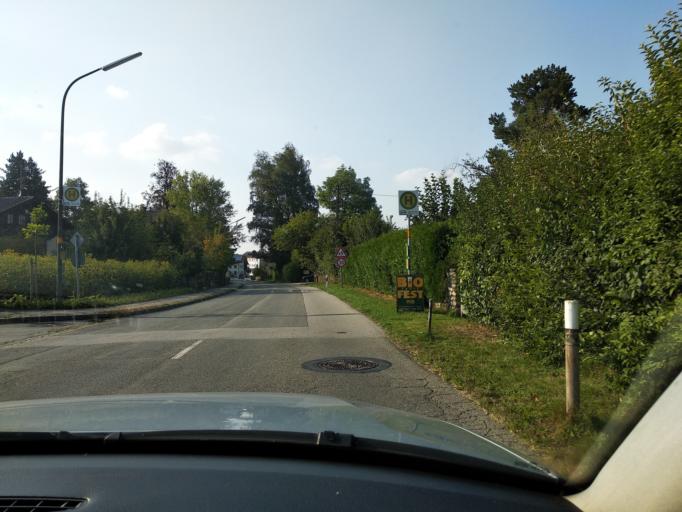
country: DE
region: Bavaria
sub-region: Upper Bavaria
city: Obing
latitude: 47.9984
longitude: 12.4112
